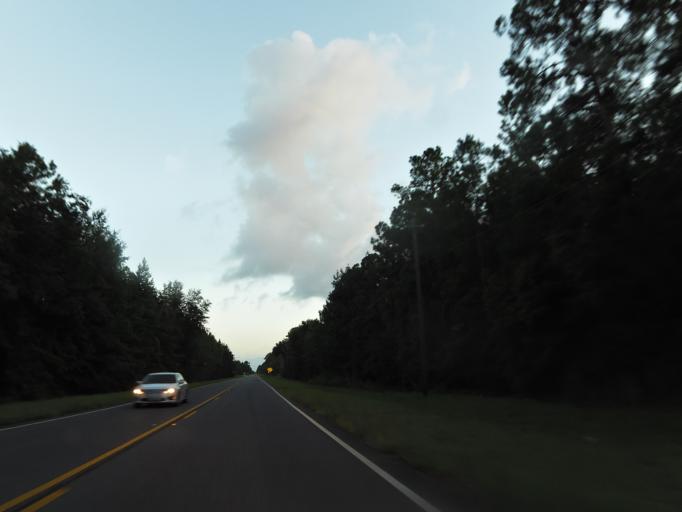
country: US
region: Georgia
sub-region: Camden County
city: Kingsland
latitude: 30.7770
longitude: -81.6868
